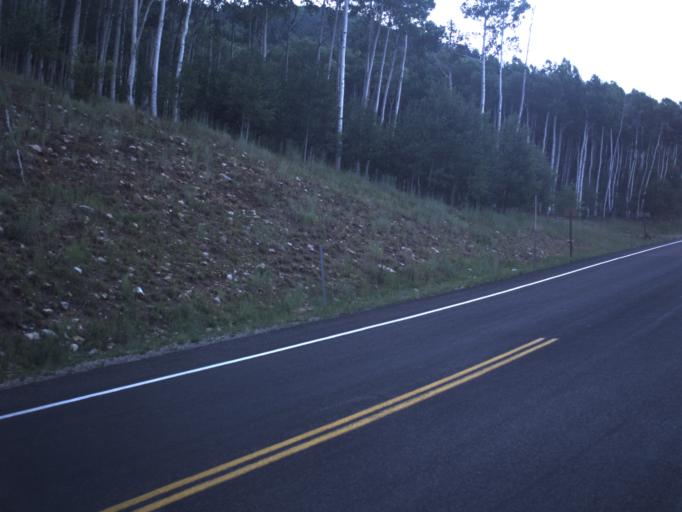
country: US
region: Utah
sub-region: Summit County
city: Francis
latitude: 40.5154
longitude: -111.0477
